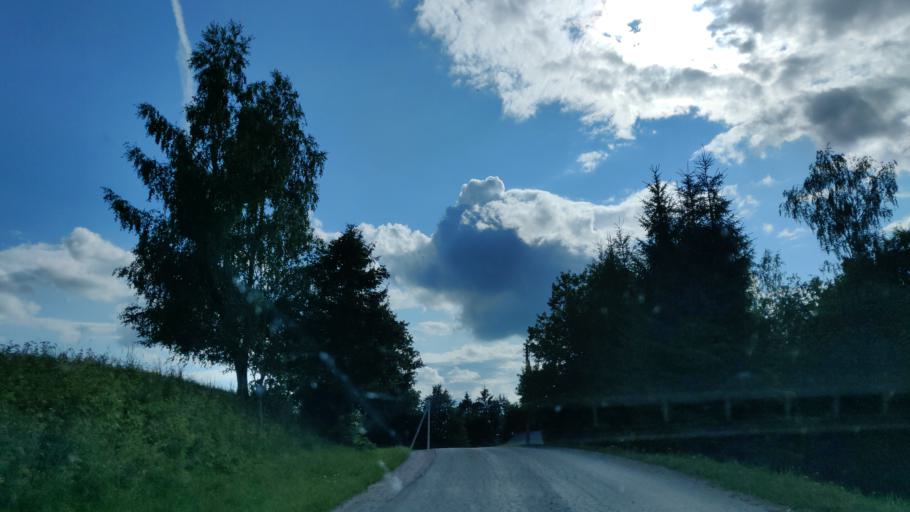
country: LT
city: Varniai
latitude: 55.5983
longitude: 22.3118
